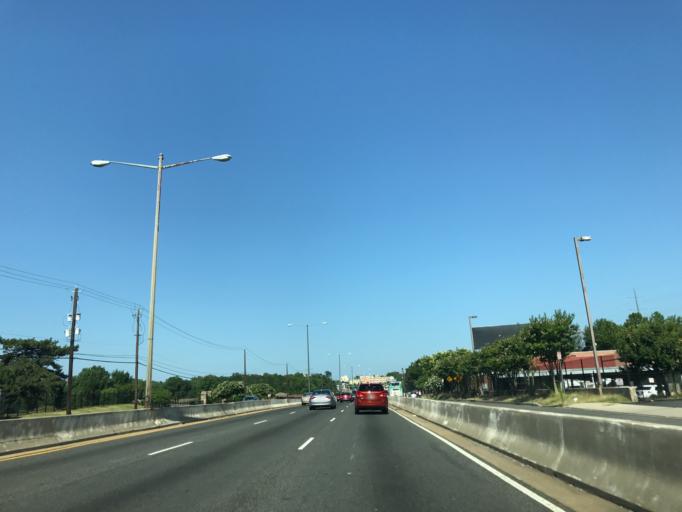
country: US
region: Maryland
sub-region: Prince George's County
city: Colmar Manor
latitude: 38.9171
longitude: -76.9629
